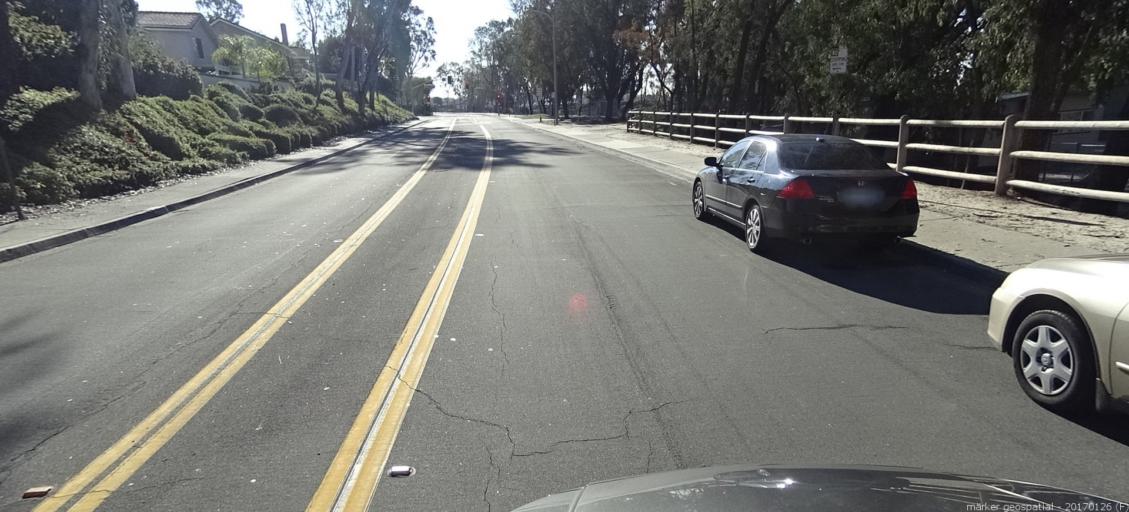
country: US
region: California
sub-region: Orange County
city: Lake Forest
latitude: 33.6409
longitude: -117.6888
